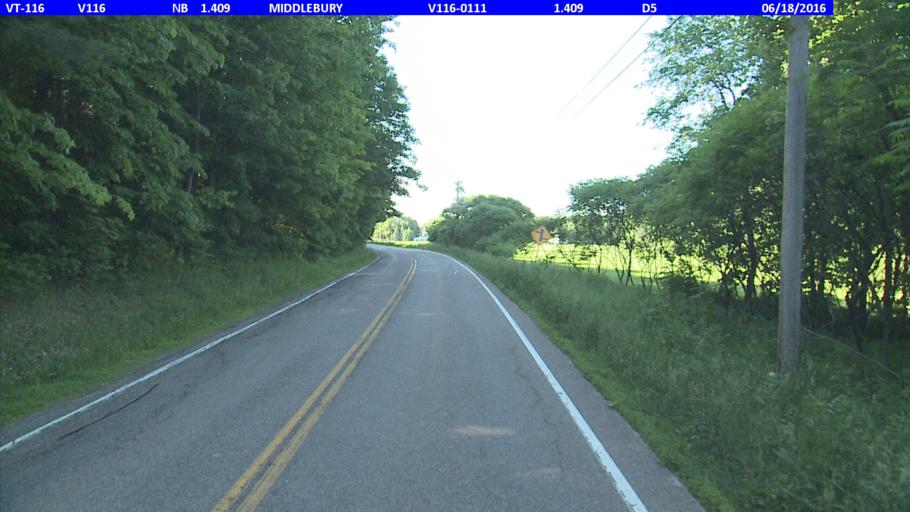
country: US
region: Vermont
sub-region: Addison County
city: Middlebury (village)
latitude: 43.9849
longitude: -73.1036
